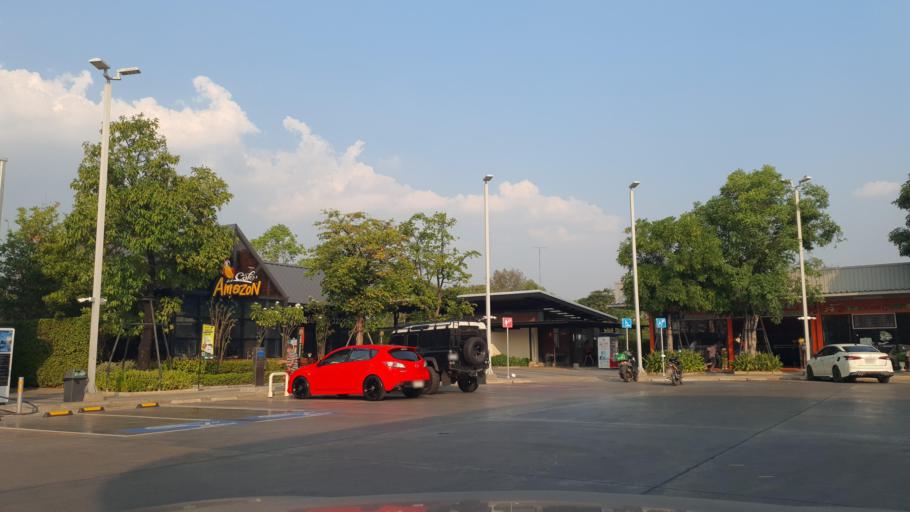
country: TH
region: Kanchanaburi
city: Kanchanaburi
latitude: 14.0545
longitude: 99.5011
